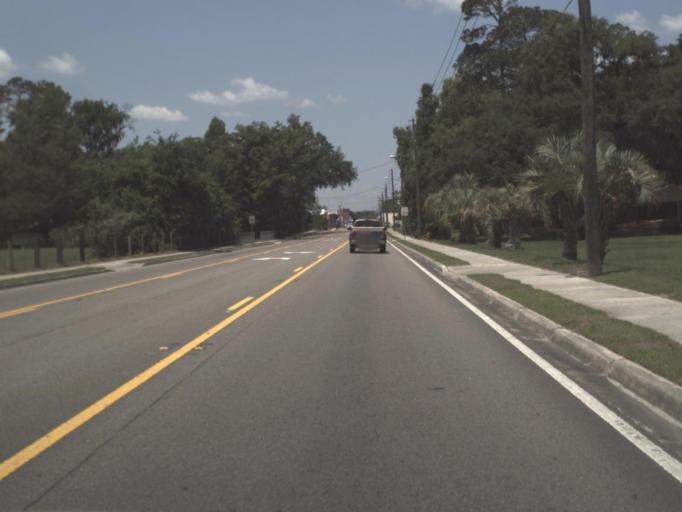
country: US
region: Florida
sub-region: Union County
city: Lake Butler
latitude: 30.0234
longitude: -82.3334
